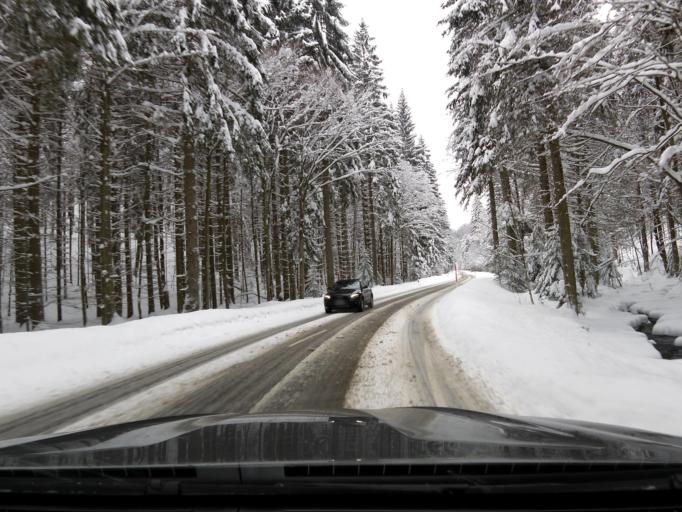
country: DE
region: Bavaria
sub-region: Lower Bavaria
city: Neuschonau
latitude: 48.9275
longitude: 13.4458
